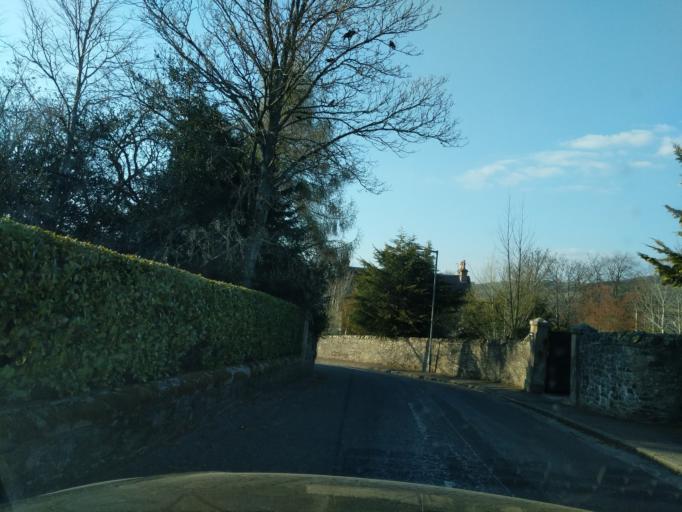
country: GB
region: Scotland
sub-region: The Scottish Borders
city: Peebles
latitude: 55.6480
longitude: -3.1957
